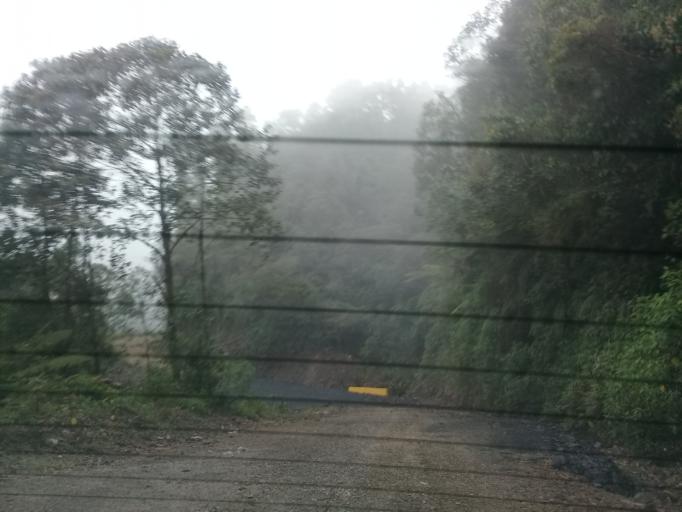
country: CO
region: Cundinamarca
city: Gachala
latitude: 4.7041
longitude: -73.4091
